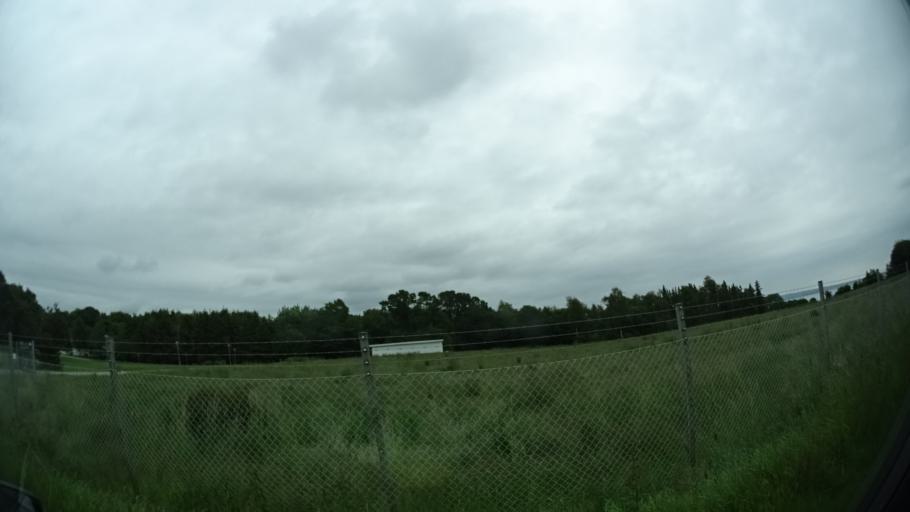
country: DK
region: Central Jutland
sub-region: Syddjurs Kommune
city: Ronde
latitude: 56.3030
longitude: 10.4108
